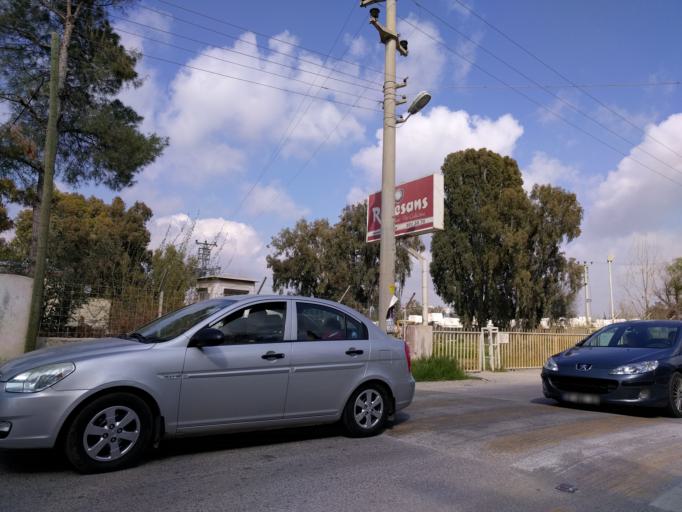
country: TR
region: Antalya
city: Cakirlar
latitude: 36.8970
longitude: 30.6111
